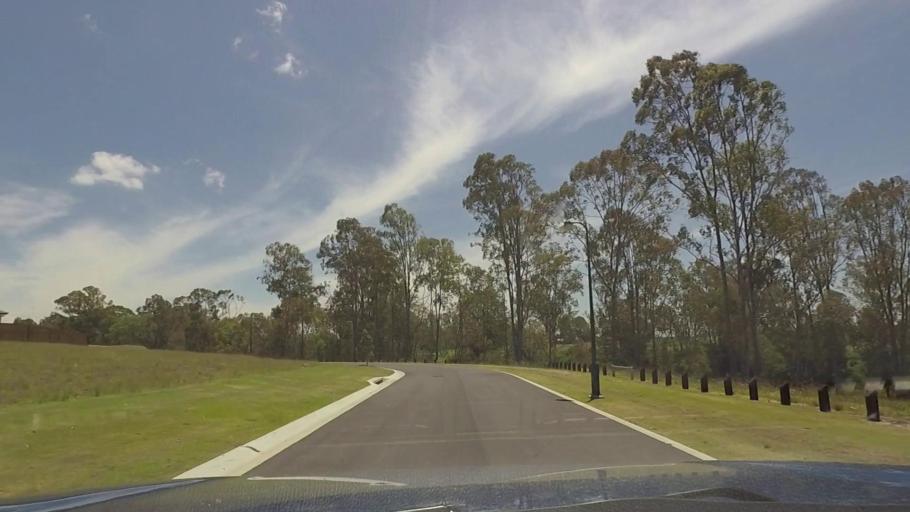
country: AU
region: Queensland
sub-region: Logan
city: Chambers Flat
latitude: -27.7697
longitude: 153.0881
